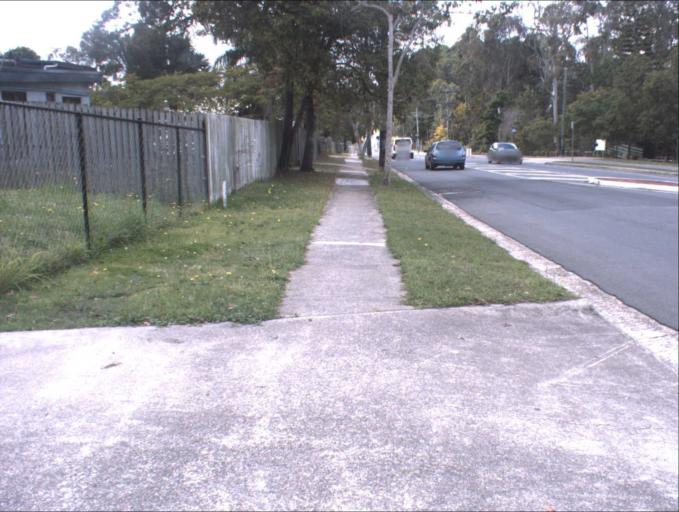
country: AU
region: Queensland
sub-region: Logan
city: Park Ridge South
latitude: -27.6867
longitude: 153.0330
